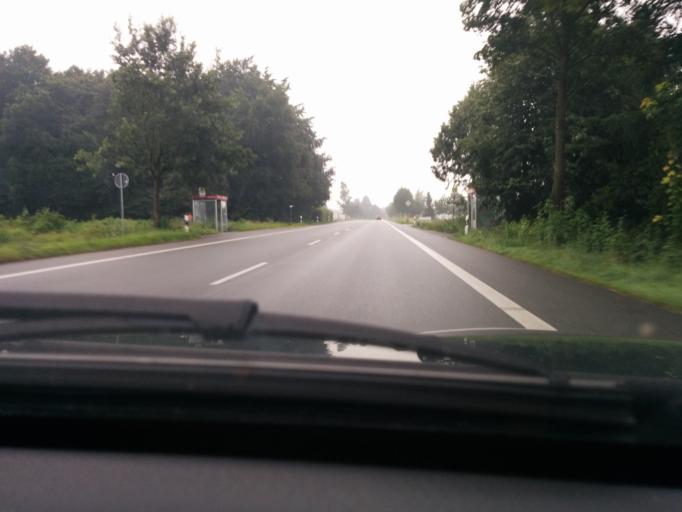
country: DE
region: North Rhine-Westphalia
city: Halle
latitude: 52.0499
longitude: 8.3788
